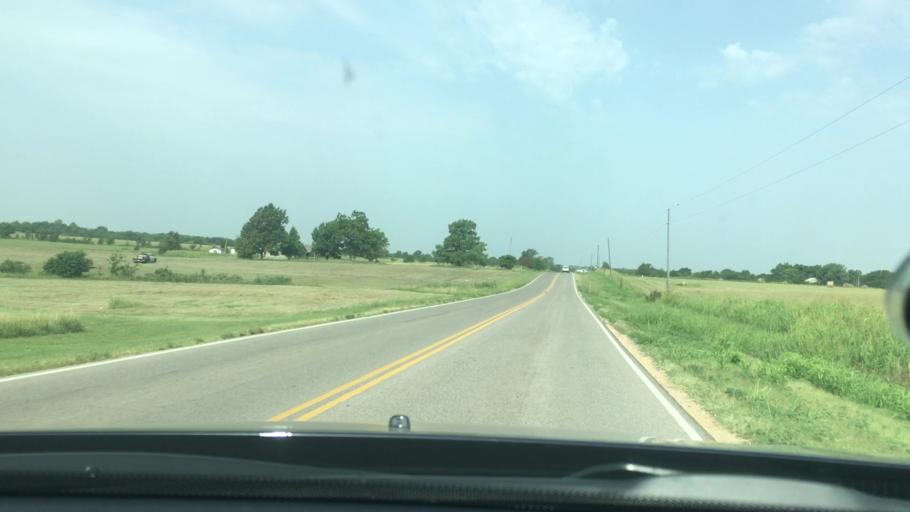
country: US
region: Oklahoma
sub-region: Garvin County
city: Stratford
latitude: 34.7967
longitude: -96.9101
